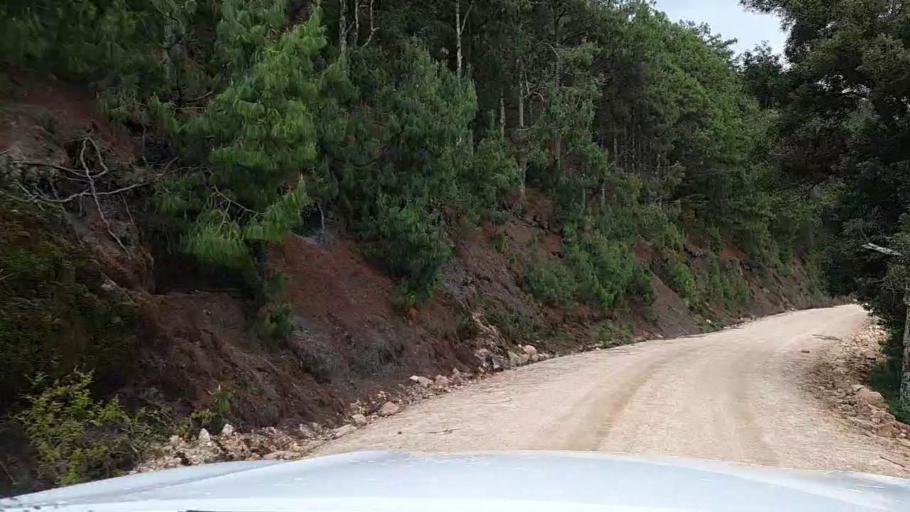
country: RW
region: Western Province
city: Kibuye
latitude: -2.3036
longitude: 29.3832
